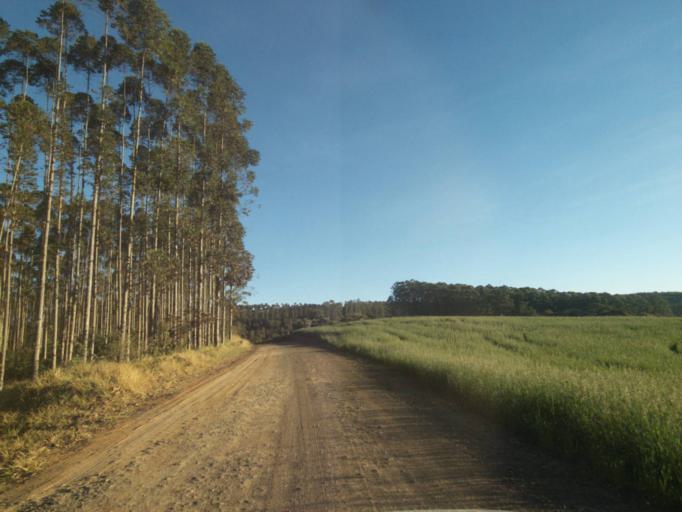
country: BR
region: Parana
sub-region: Telemaco Borba
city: Telemaco Borba
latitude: -24.4882
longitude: -50.5939
